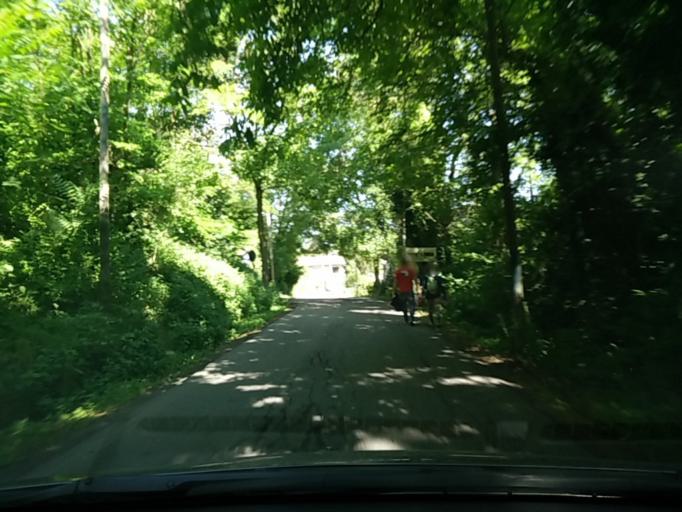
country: IT
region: Lombardy
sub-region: Provincia di Pavia
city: Godiasco
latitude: 44.9048
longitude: 9.0416
